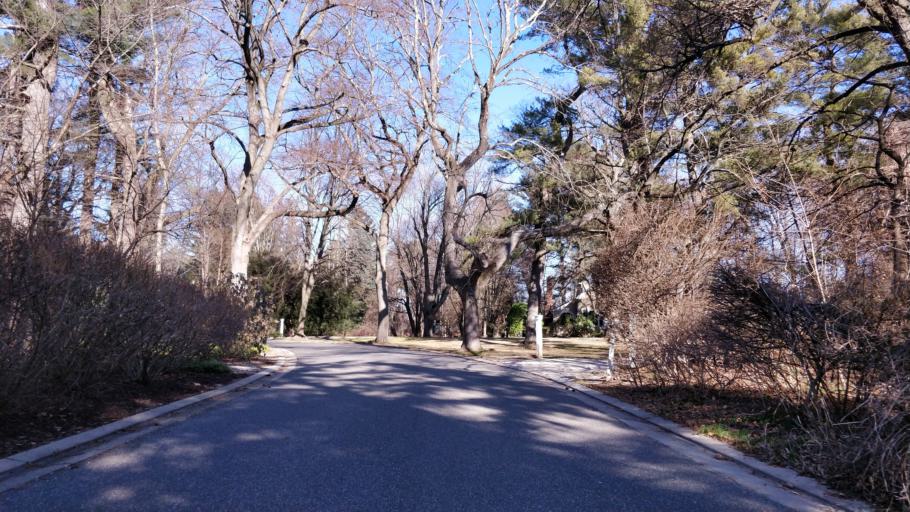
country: US
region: New York
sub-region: Nassau County
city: Old Brookville
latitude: 40.8219
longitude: -73.6101
